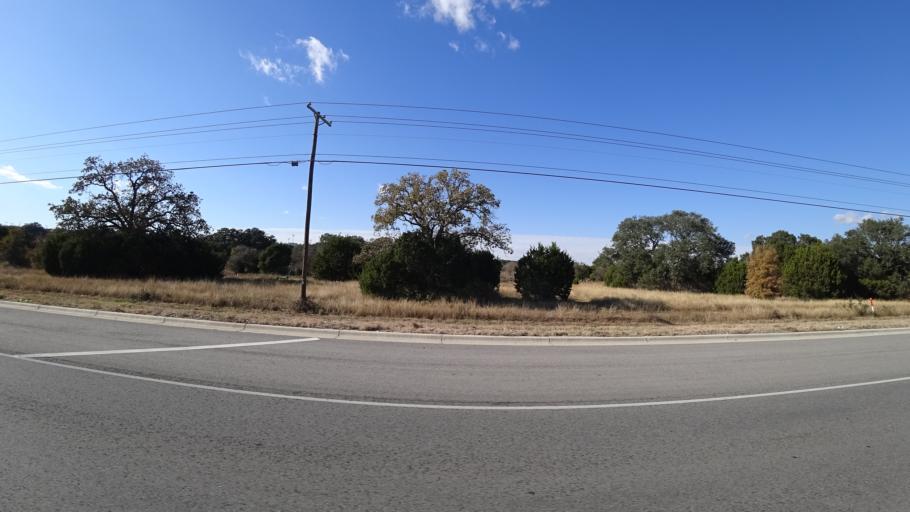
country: US
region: Texas
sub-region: Williamson County
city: Brushy Creek
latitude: 30.4907
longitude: -97.7280
